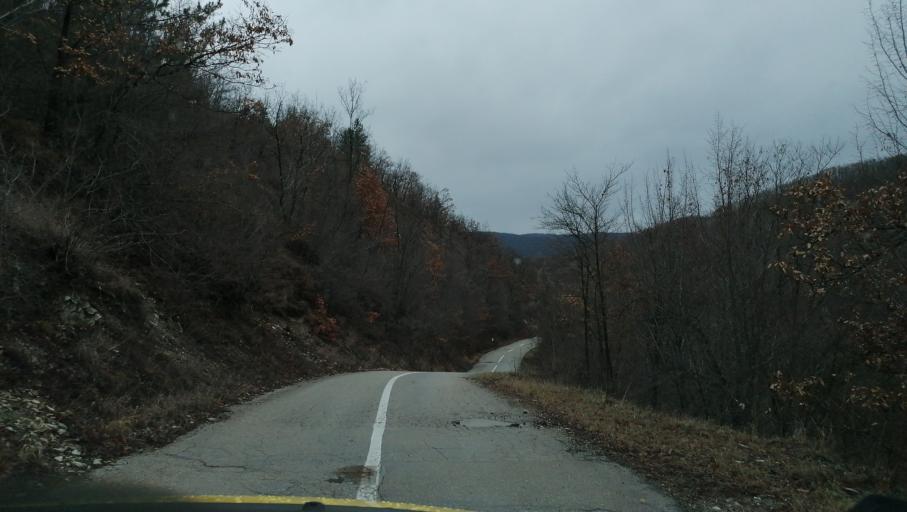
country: RS
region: Central Serbia
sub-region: Pirotski Okrug
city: Dimitrovgrad
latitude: 42.9558
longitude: 22.7806
